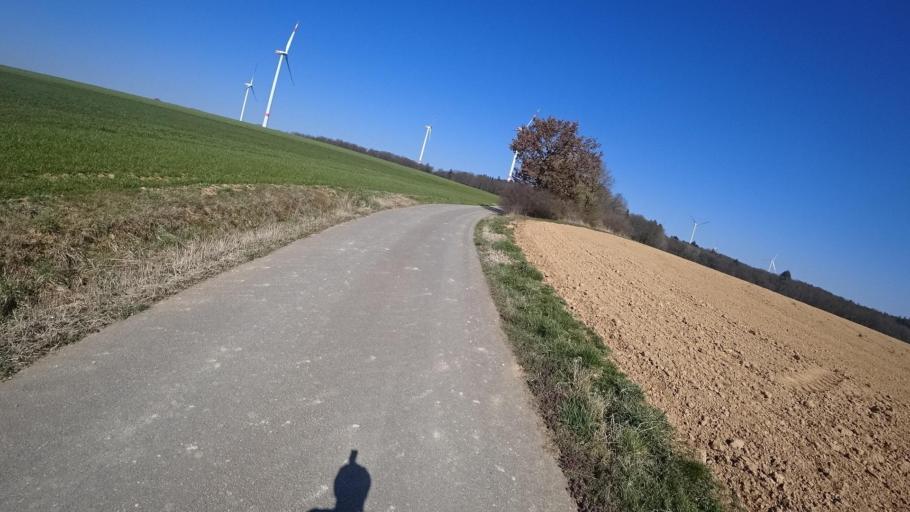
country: DE
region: Rheinland-Pfalz
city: Rayerschied
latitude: 50.0232
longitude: 7.5897
